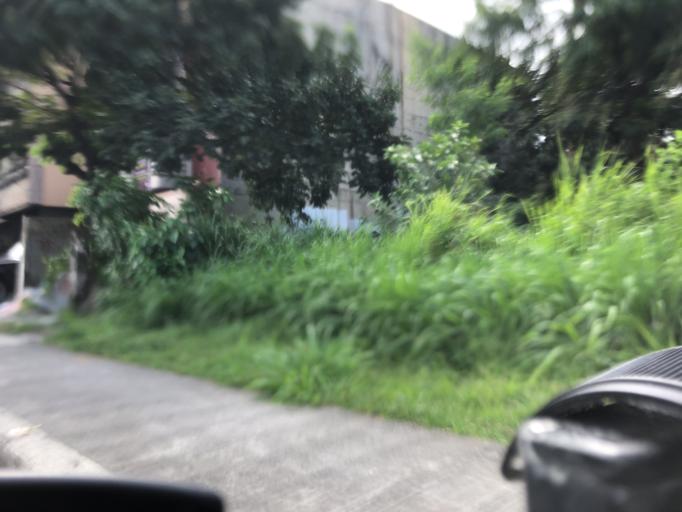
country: PH
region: Calabarzon
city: Bagong Pagasa
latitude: 14.7204
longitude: 121.0612
